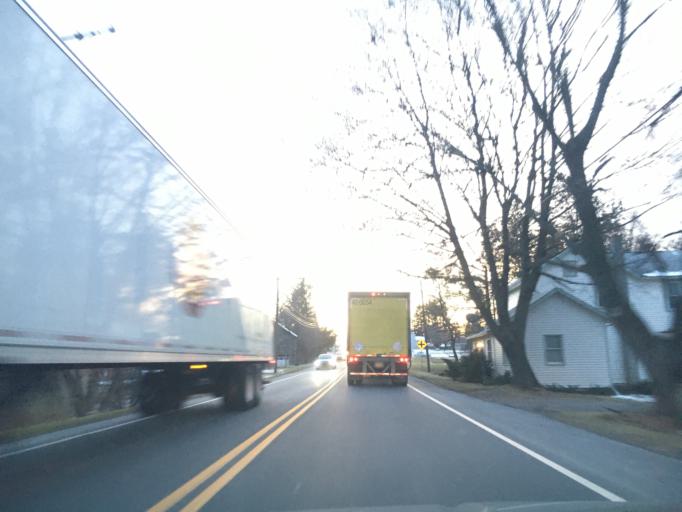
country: US
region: Pennsylvania
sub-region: Northampton County
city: Wind Gap
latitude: 40.8027
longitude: -75.3451
